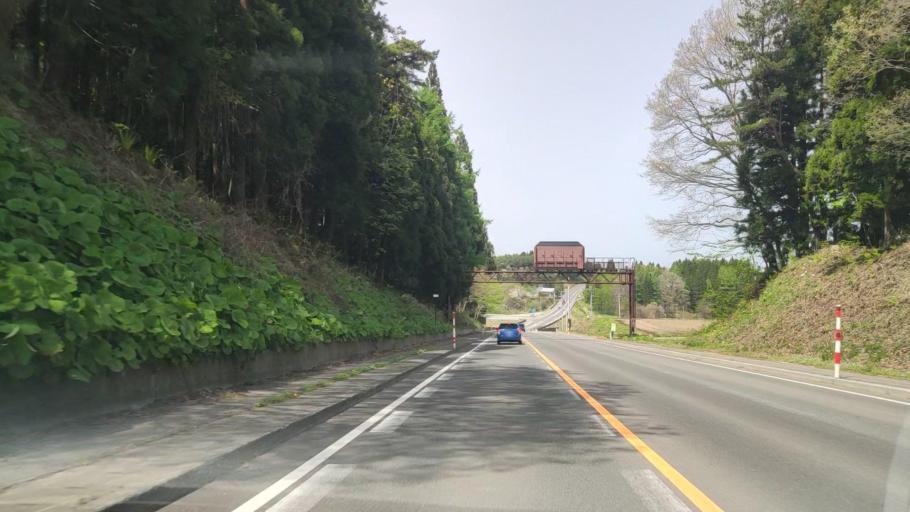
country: JP
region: Aomori
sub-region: Misawa Shi
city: Inuotose
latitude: 40.6613
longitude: 141.1895
